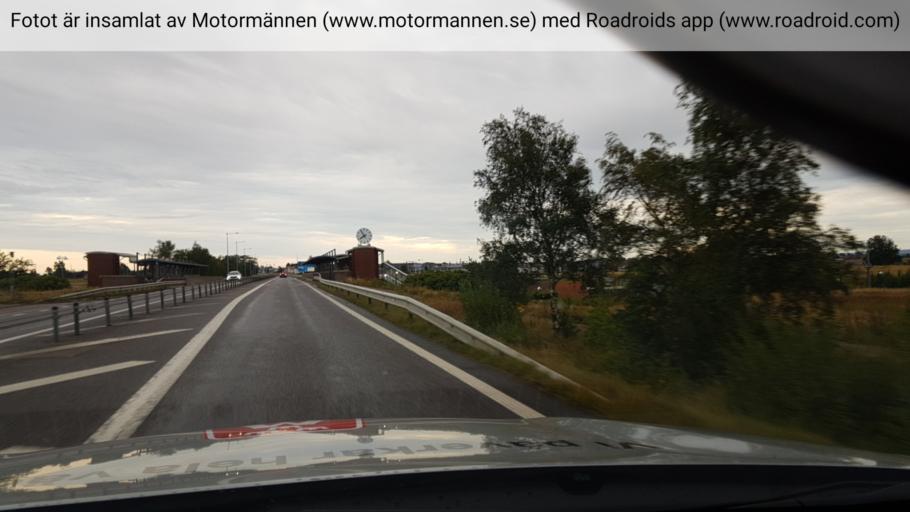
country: SE
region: Halland
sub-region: Laholms Kommun
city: Laholm
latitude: 56.5032
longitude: 12.9967
